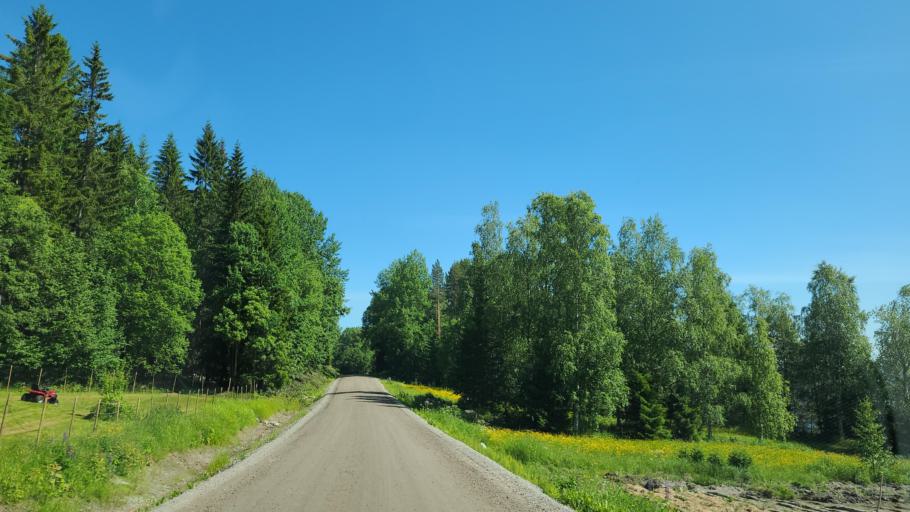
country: SE
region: Vaesterbotten
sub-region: Bjurholms Kommun
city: Bjurholm
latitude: 63.6765
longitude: 19.0126
